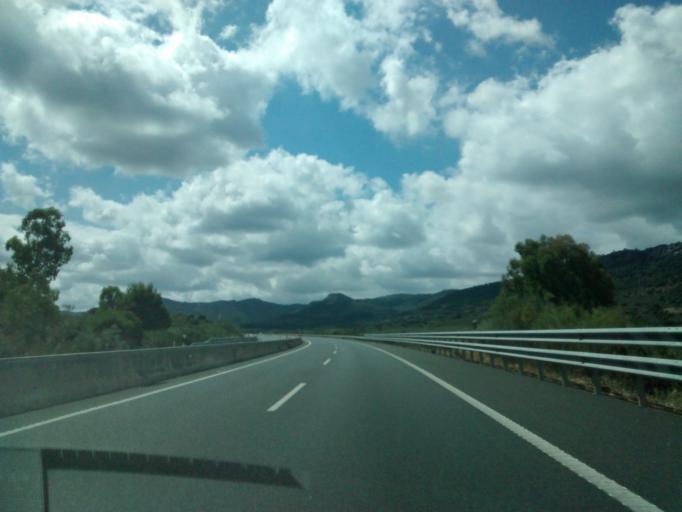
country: ES
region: Extremadura
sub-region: Provincia de Caceres
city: Romangordo
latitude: 39.7197
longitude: -5.7103
